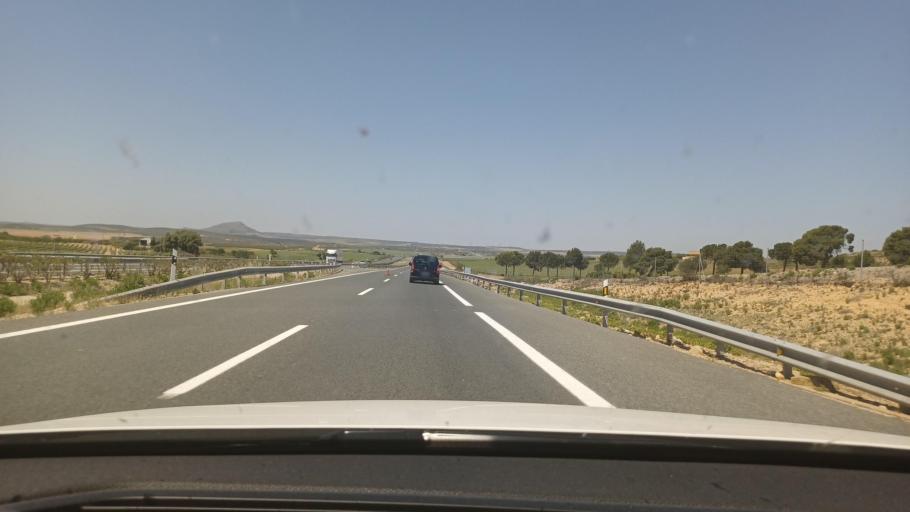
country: ES
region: Castille-La Mancha
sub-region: Provincia de Albacete
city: Alpera
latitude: 38.8799
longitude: -1.2029
